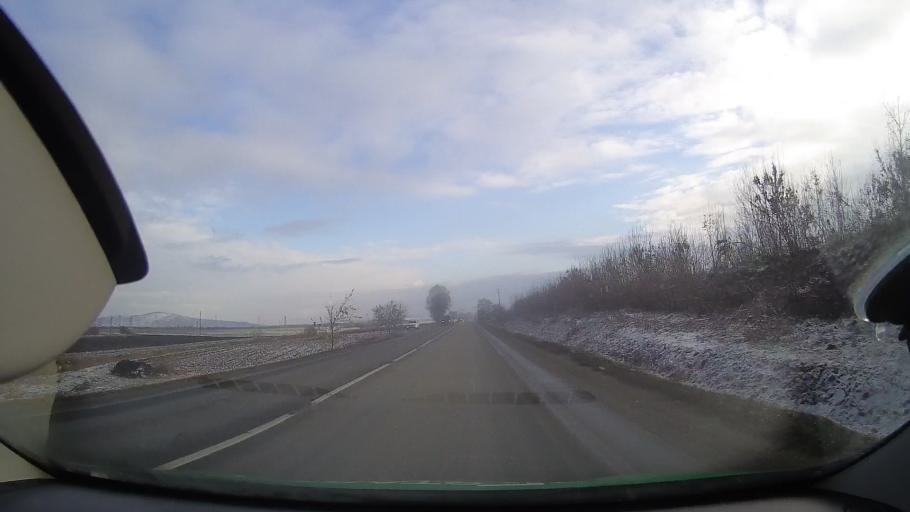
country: RO
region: Mures
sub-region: Comuna Cuci
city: Cuci
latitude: 46.4600
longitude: 24.1665
